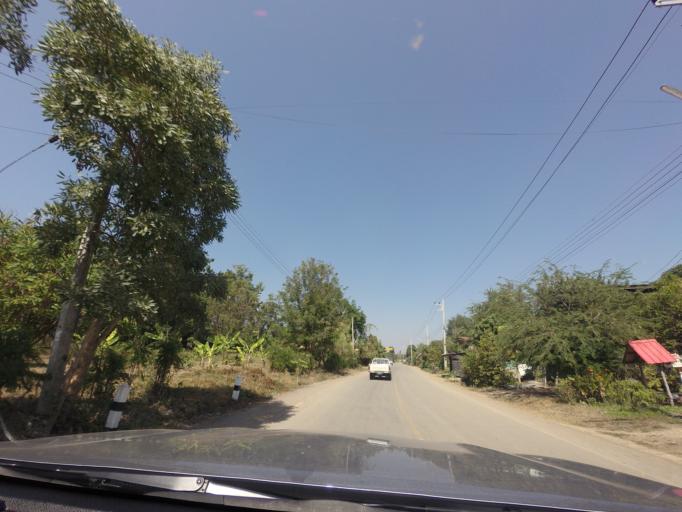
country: TH
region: Sukhothai
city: Si Samrong
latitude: 17.1643
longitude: 99.7701
